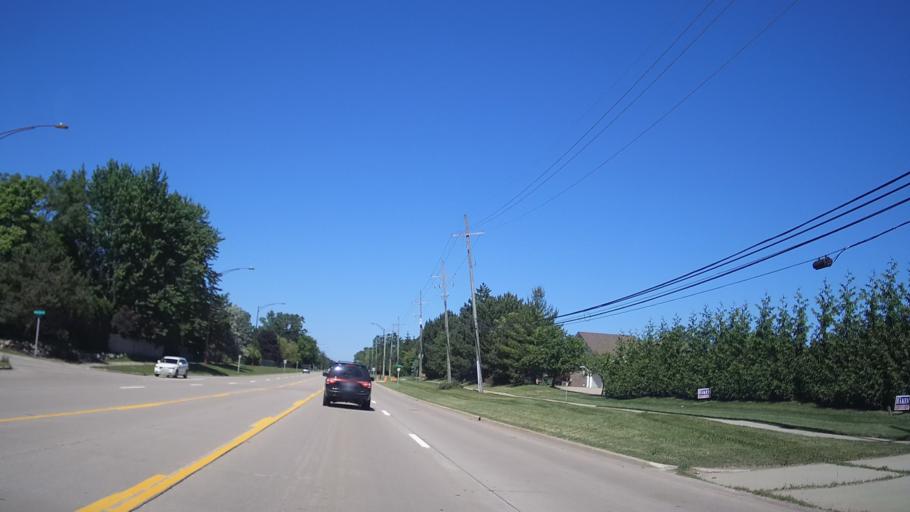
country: US
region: Michigan
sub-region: Oakland County
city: Troy
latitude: 42.5929
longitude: -83.0973
